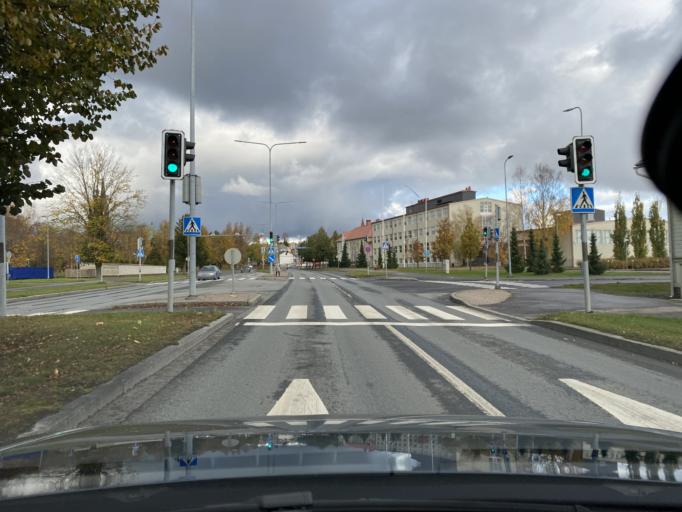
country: FI
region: Haeme
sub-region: Forssa
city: Forssa
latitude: 60.8130
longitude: 23.6330
